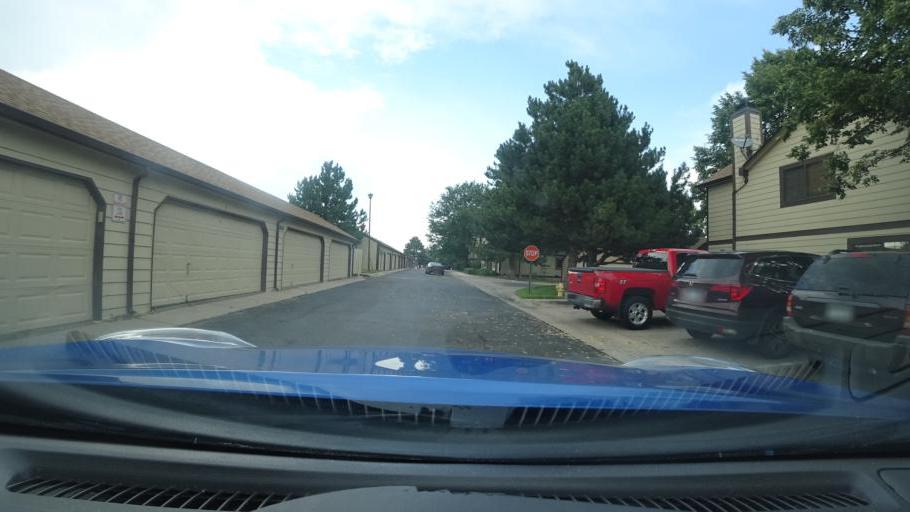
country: US
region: Colorado
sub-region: Adams County
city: Aurora
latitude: 39.6838
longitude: -104.7861
